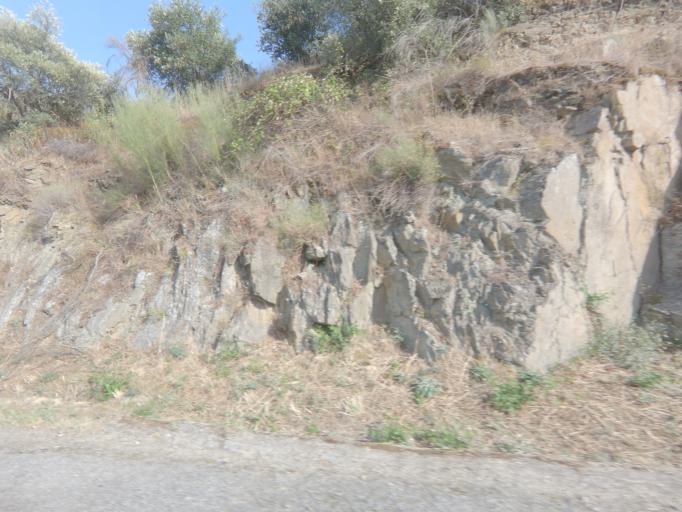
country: PT
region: Viseu
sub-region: Tabuaco
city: Tabuaco
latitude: 41.1661
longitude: -7.5633
